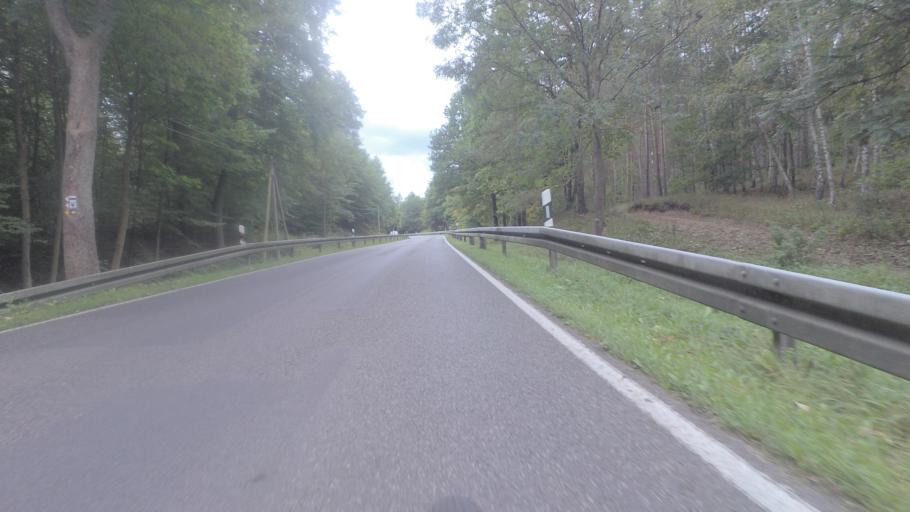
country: DE
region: Brandenburg
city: Eberswalde
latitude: 52.8091
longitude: 13.7701
